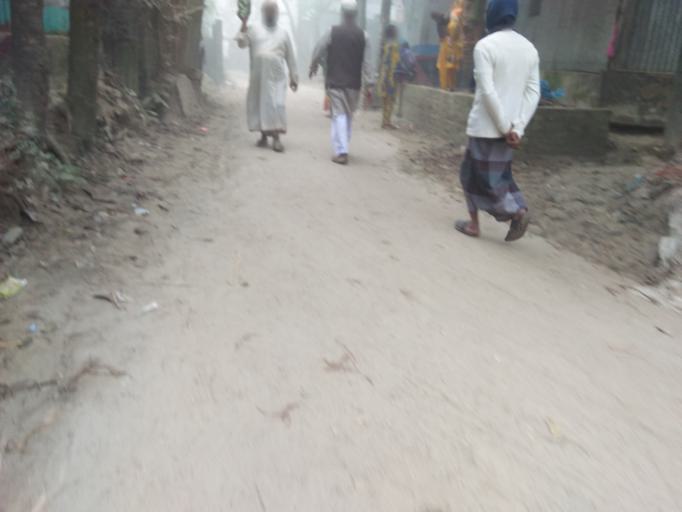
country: BD
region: Dhaka
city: Azimpur
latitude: 23.6880
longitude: 90.3024
